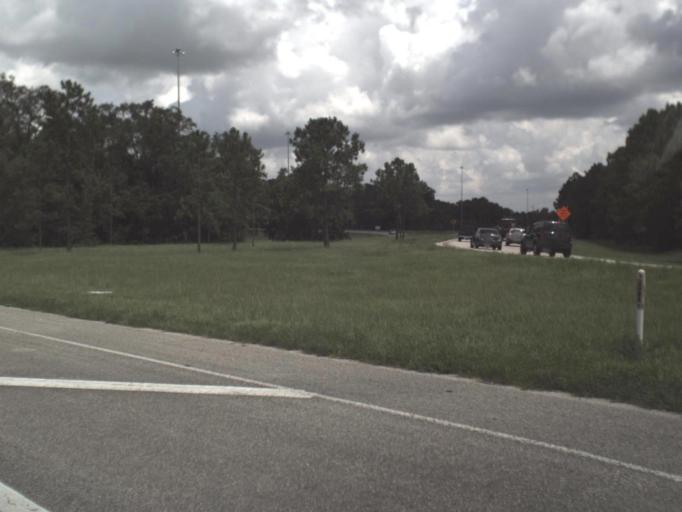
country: US
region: Florida
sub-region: Hillsborough County
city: Temple Terrace
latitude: 28.0541
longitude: -82.3579
